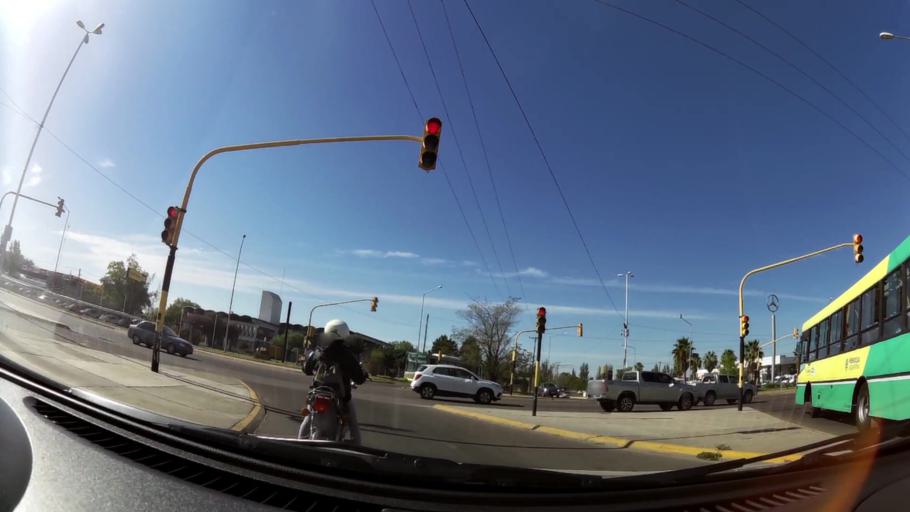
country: AR
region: Mendoza
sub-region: Departamento de Godoy Cruz
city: Godoy Cruz
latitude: -32.9322
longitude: -68.7983
